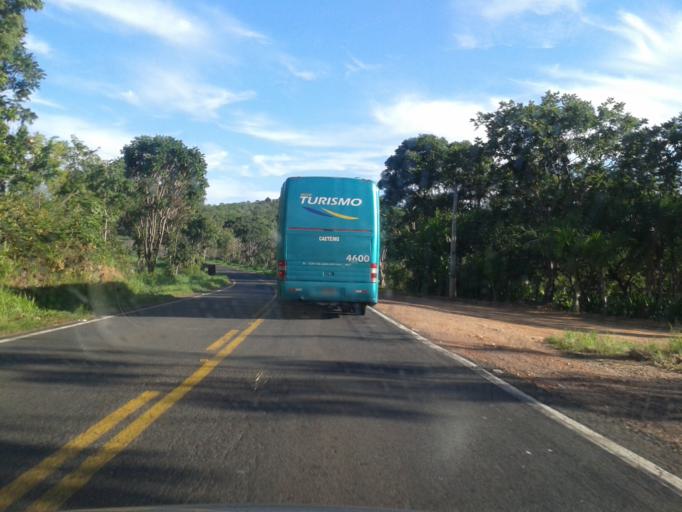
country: BR
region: Minas Gerais
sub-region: Tupaciguara
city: Tupaciguara
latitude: -18.3072
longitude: -48.5610
